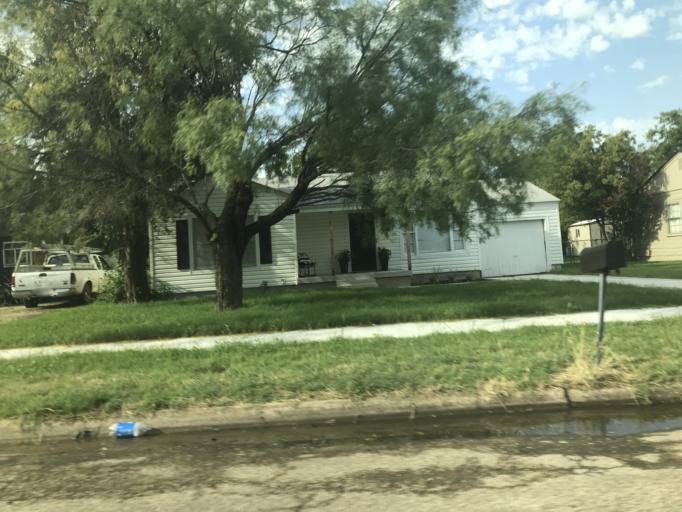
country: US
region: Texas
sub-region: Taylor County
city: Abilene
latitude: 32.4288
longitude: -99.7610
